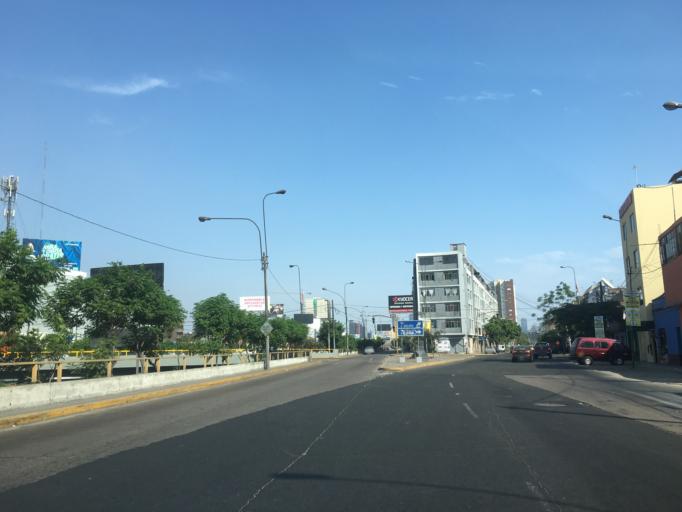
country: PE
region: Lima
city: Lima
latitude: -12.0729
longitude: -77.0308
